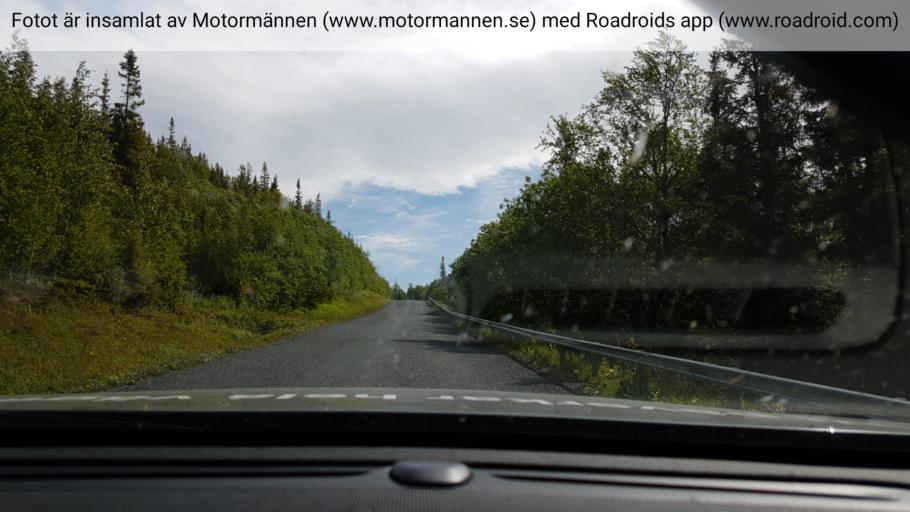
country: SE
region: Vaesterbotten
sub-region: Vilhelmina Kommun
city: Sjoberg
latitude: 65.2388
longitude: 15.4473
